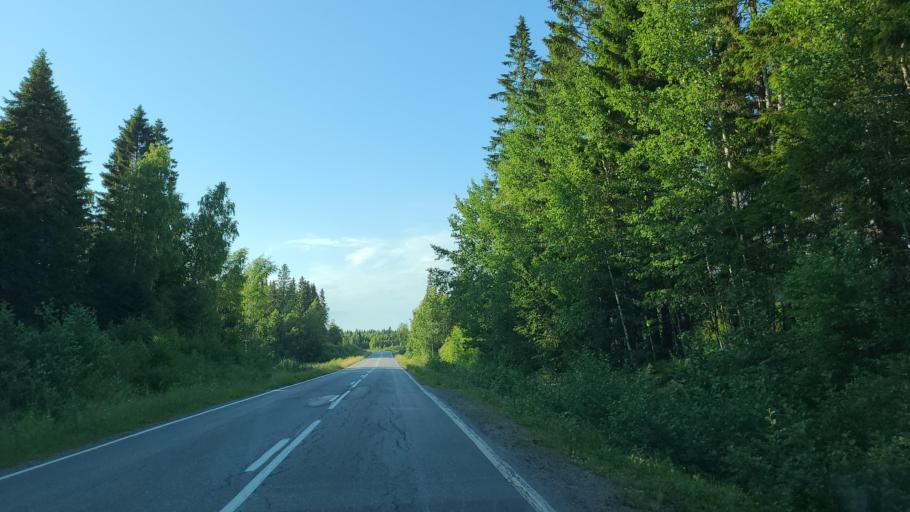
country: FI
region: Ostrobothnia
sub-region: Vaasa
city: Replot
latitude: 63.3166
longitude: 21.3578
